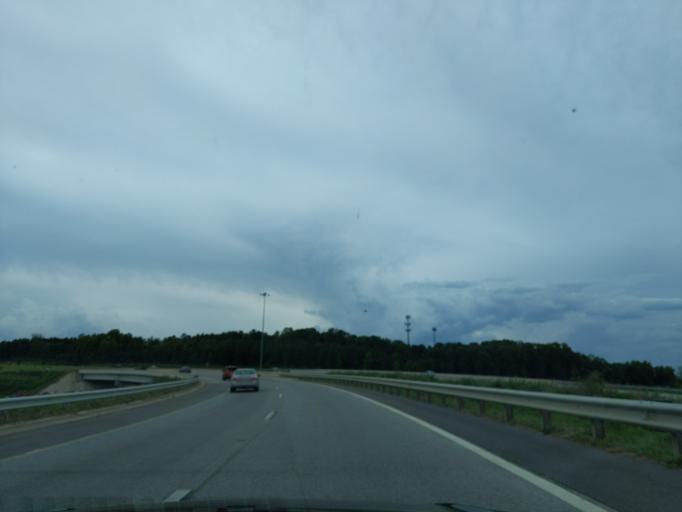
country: US
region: North Carolina
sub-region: Cabarrus County
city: Harrisburg
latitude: 35.3494
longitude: -80.7310
